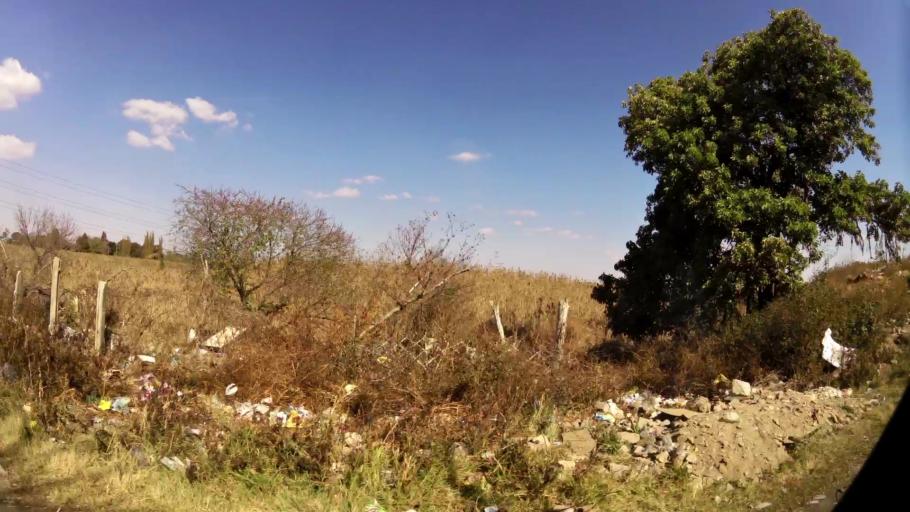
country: ZA
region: Gauteng
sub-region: City of Johannesburg Metropolitan Municipality
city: Soweto
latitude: -26.2458
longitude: 27.9037
